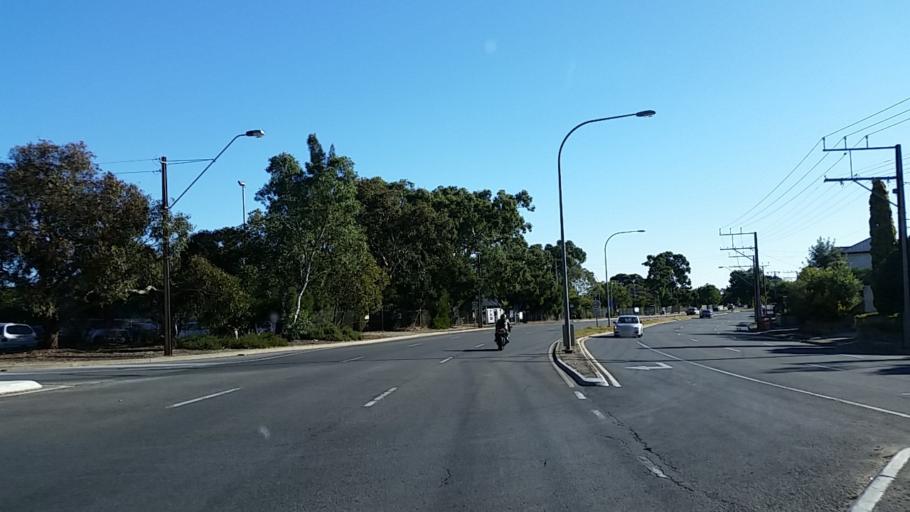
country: AU
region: South Australia
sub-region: Tea Tree Gully
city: Hope Valley
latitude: -34.8268
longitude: 138.7066
